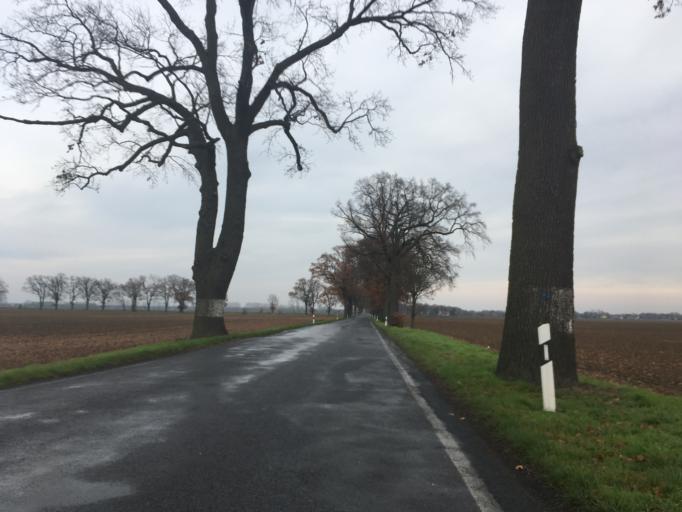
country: DE
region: Brandenburg
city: Letschin
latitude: 52.6685
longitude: 14.3843
